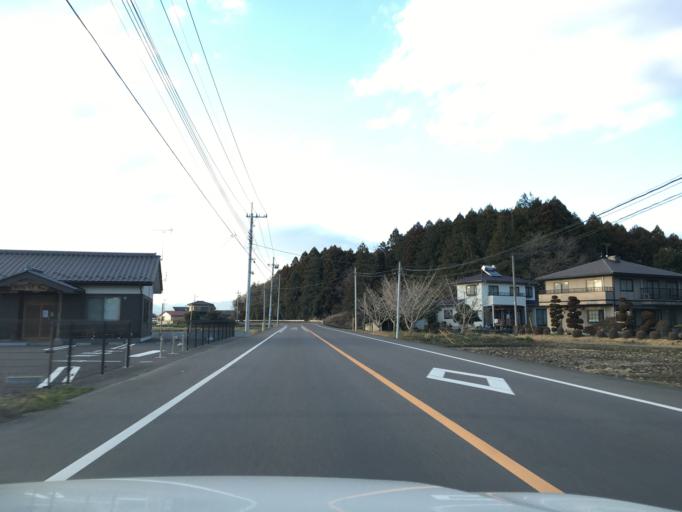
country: JP
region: Tochigi
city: Otawara
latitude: 36.8737
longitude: 140.0729
